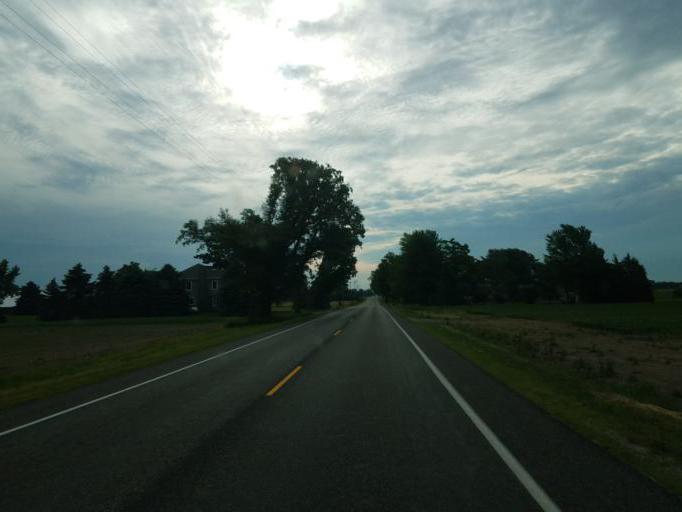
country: US
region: Michigan
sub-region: Eaton County
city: Charlotte
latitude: 42.6264
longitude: -84.8512
